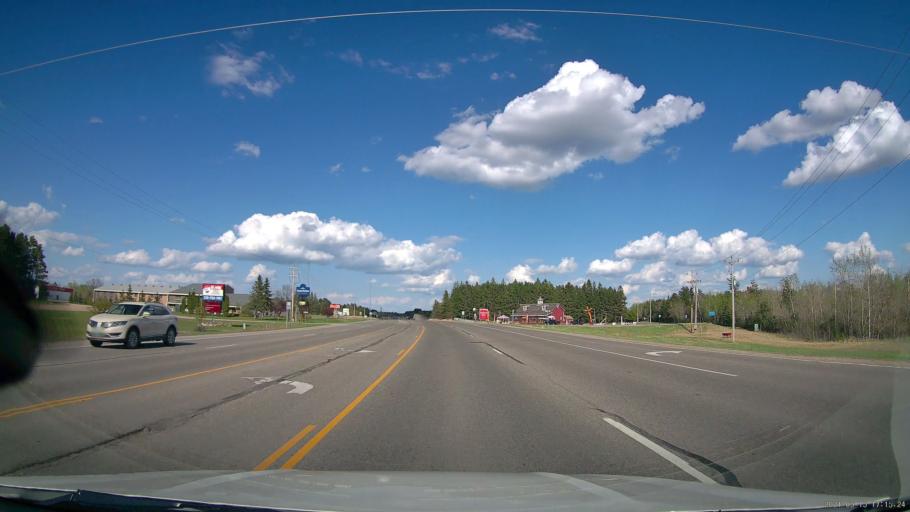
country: US
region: Minnesota
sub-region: Hubbard County
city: Park Rapids
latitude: 46.9222
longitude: -95.0279
